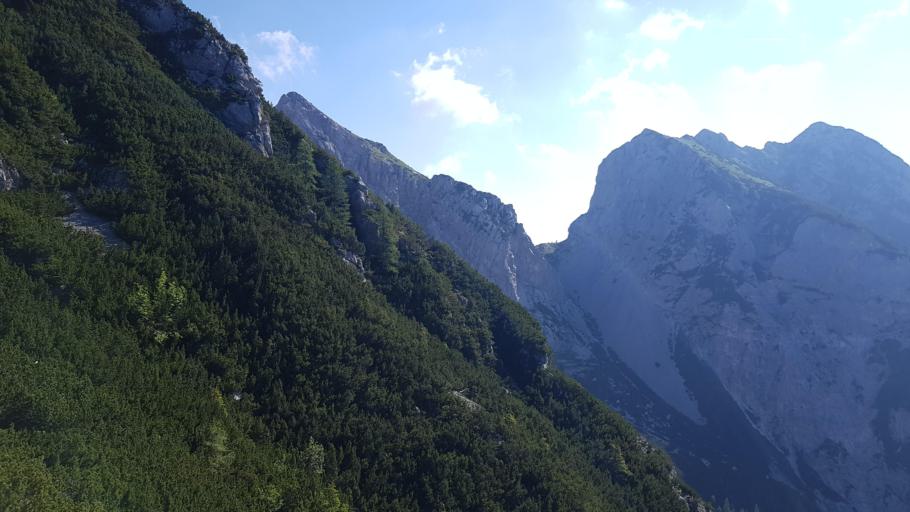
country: IT
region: Friuli Venezia Giulia
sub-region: Provincia di Udine
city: Malborghetto
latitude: 46.4706
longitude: 13.4157
